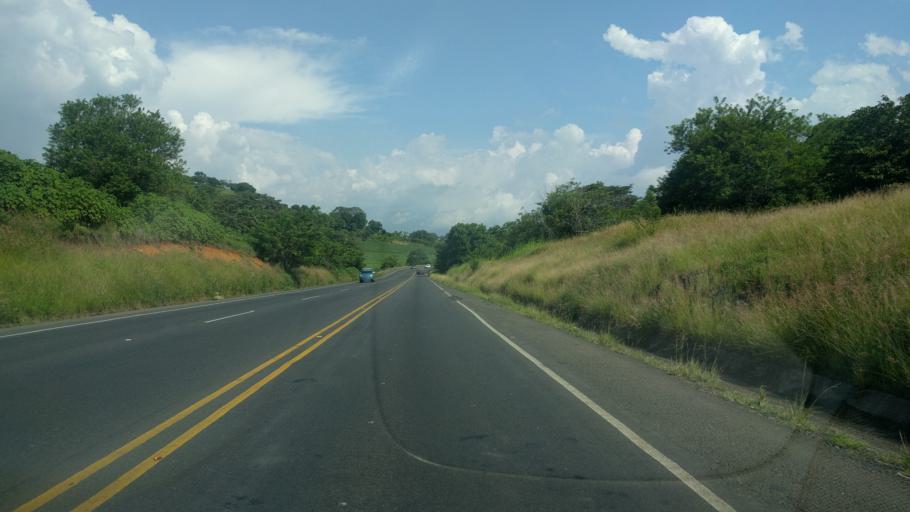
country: CR
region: Alajuela
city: Carrillos
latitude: 10.0062
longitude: -84.3206
